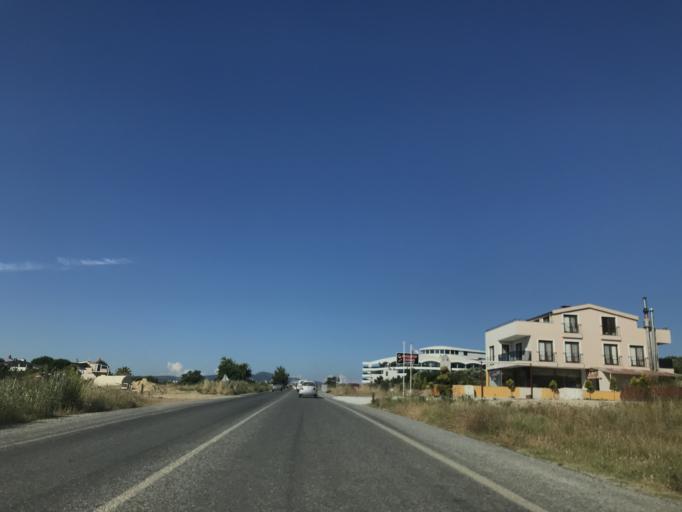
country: TR
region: Aydin
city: Davutlar
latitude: 37.7256
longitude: 27.2614
